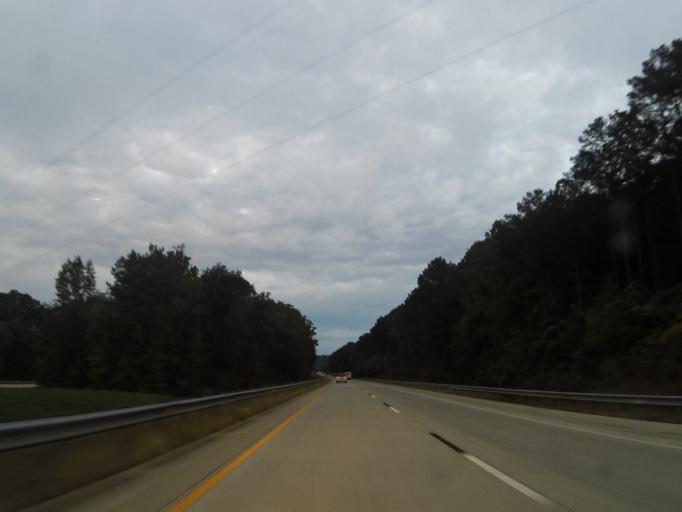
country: US
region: Alabama
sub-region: Etowah County
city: Attalla
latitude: 34.0393
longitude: -86.0672
